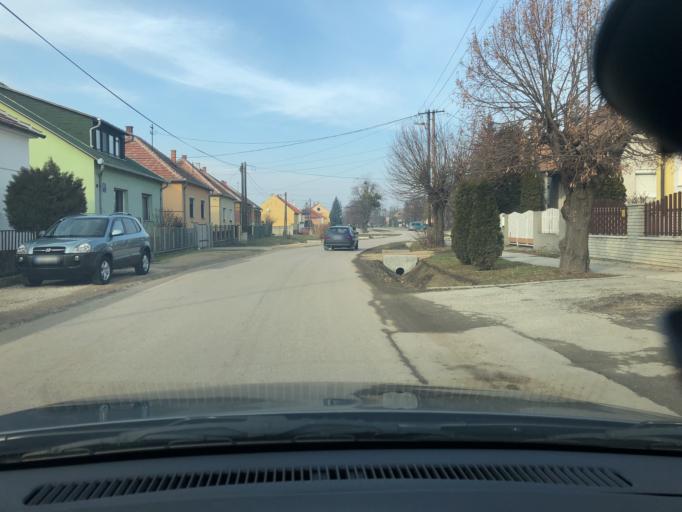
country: HU
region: Gyor-Moson-Sopron
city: Kapuvar
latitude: 47.5876
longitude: 17.0212
